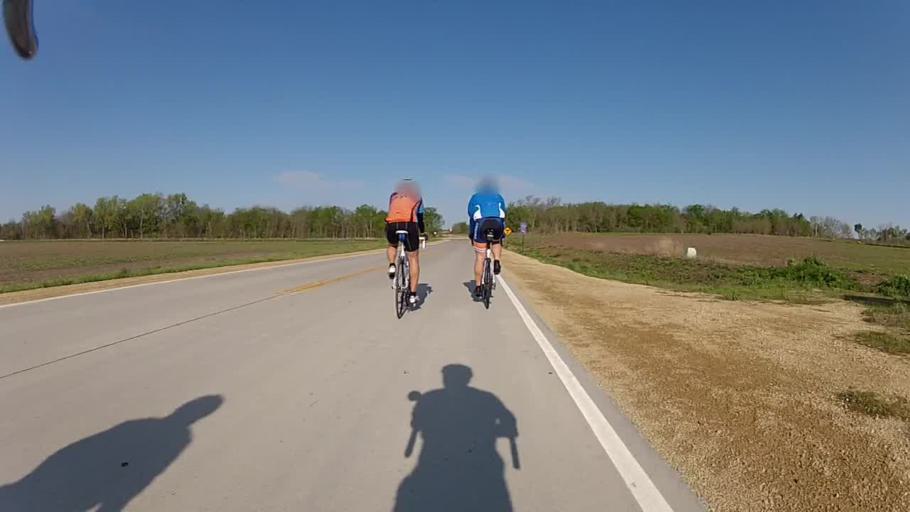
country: US
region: Kansas
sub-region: Riley County
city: Ogden
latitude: 39.1533
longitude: -96.6804
